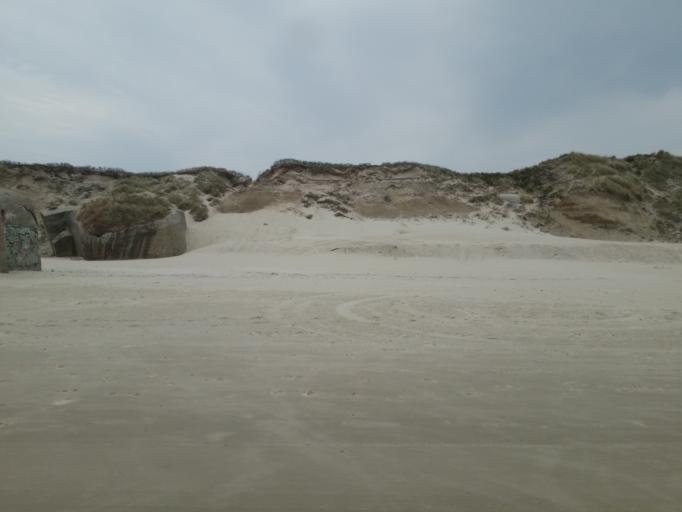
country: DK
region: North Denmark
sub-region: Jammerbugt Kommune
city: Pandrup
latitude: 57.3816
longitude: 9.7183
